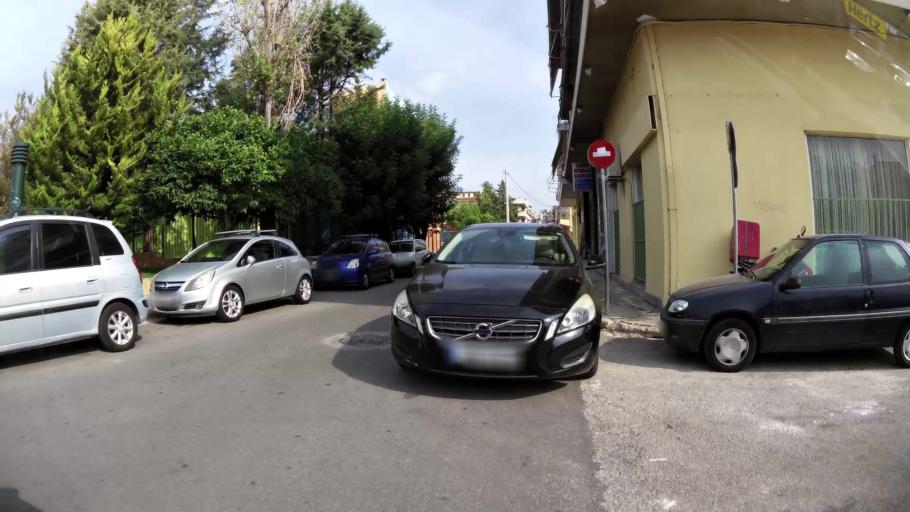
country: GR
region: Attica
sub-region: Nomarchia Athinas
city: Petroupolis
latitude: 38.0275
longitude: 23.6808
